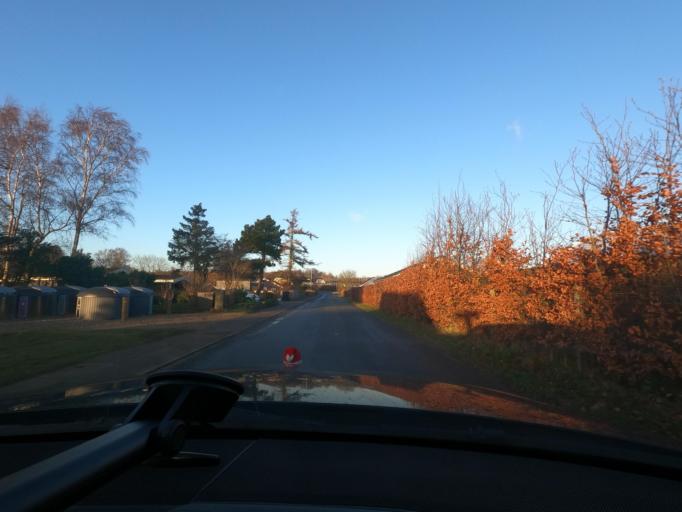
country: DK
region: South Denmark
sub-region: Sonderborg Kommune
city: Broager
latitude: 54.9004
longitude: 9.7018
